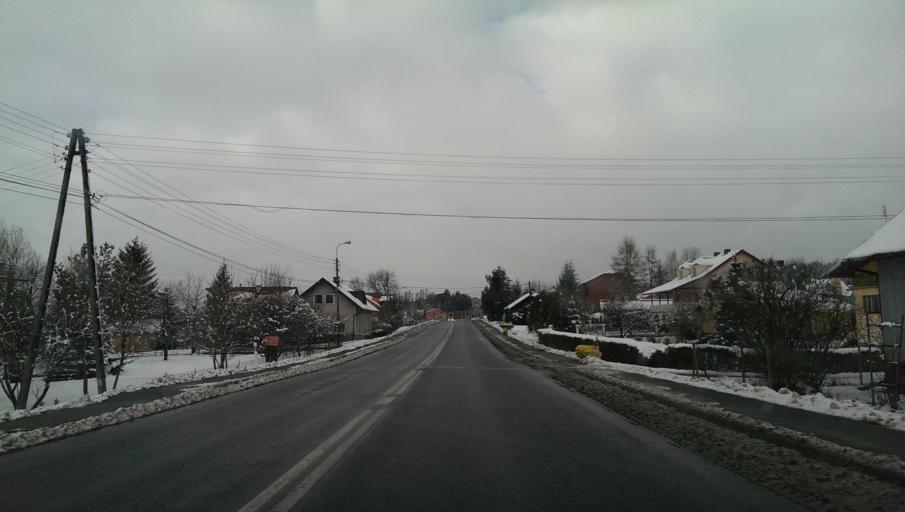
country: PL
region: Subcarpathian Voivodeship
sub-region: Powiat brzozowski
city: Humniska
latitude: 49.6830
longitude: 22.0414
